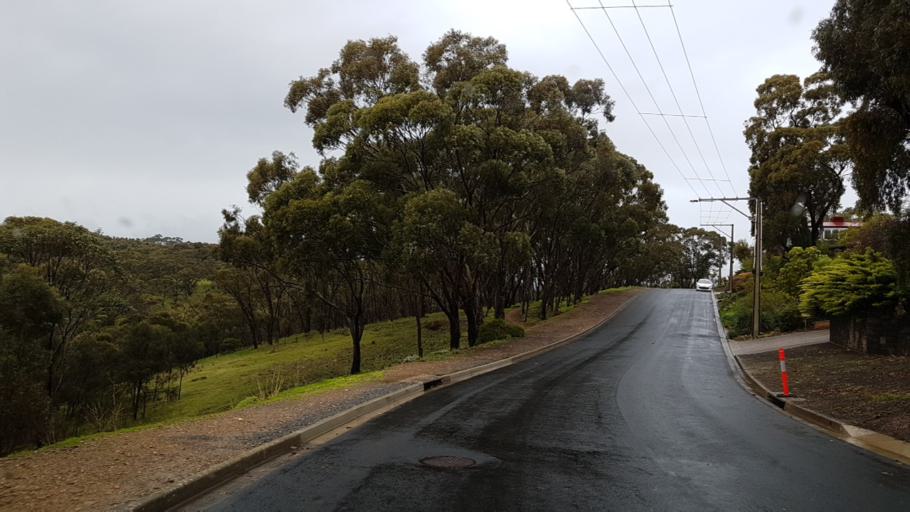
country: AU
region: South Australia
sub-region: Onkaparinga
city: Bedford Park
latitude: -35.0386
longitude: 138.5843
